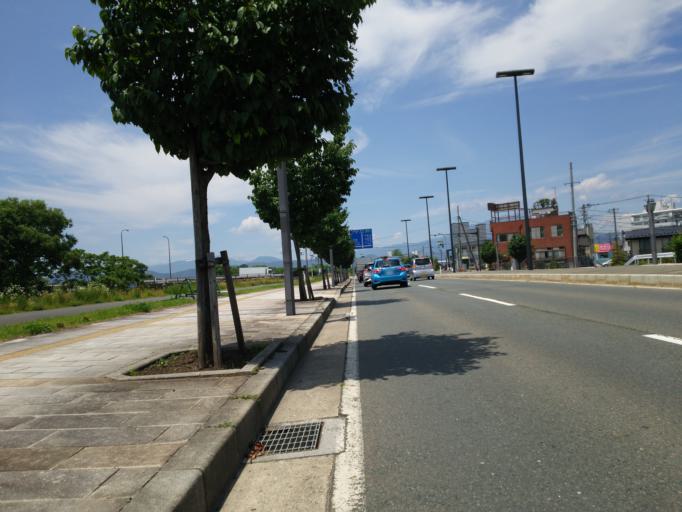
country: JP
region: Iwate
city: Morioka-shi
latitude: 39.7029
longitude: 141.1257
